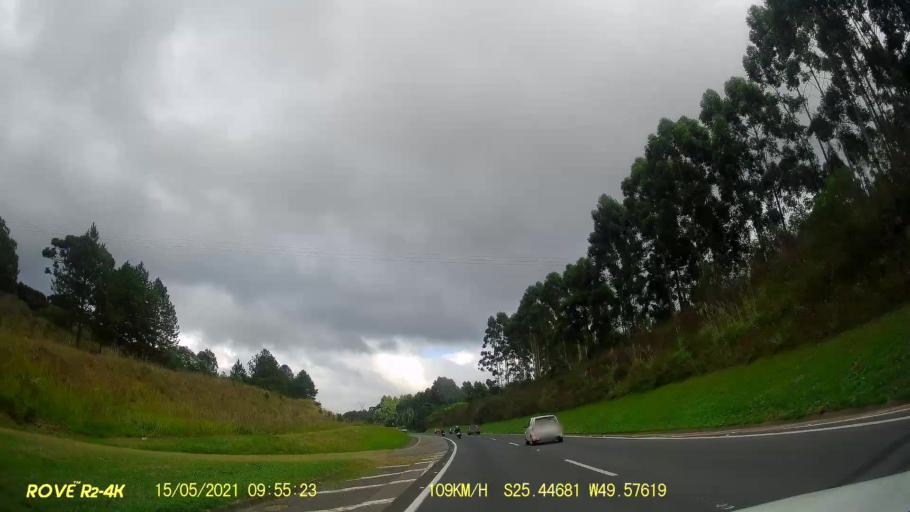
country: BR
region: Parana
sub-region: Campo Largo
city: Campo Largo
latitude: -25.4466
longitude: -49.5766
